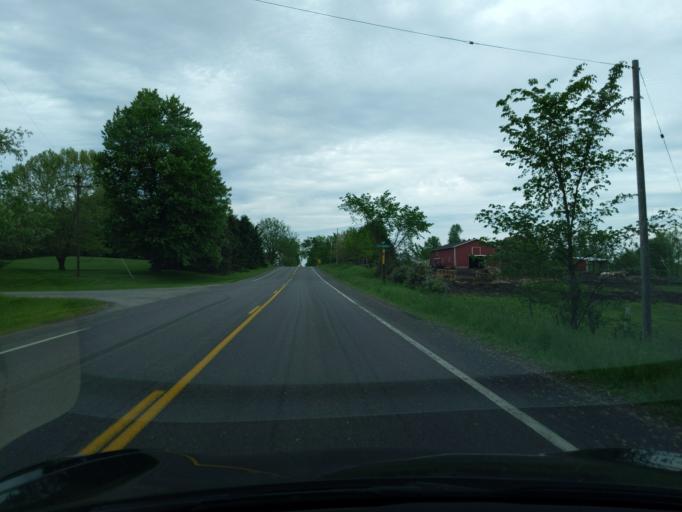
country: US
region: Michigan
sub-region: Ingham County
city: Mason
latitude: 42.5814
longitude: -84.3572
